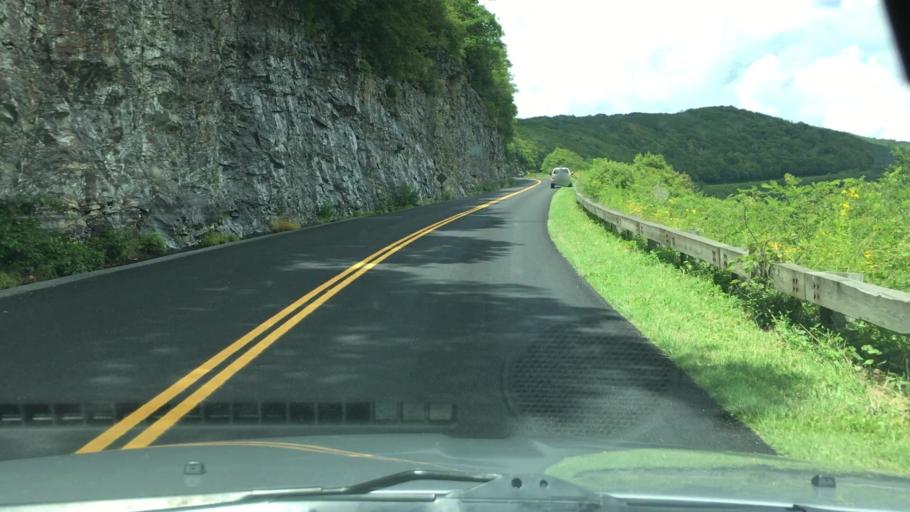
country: US
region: North Carolina
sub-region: Buncombe County
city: Swannanoa
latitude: 35.6889
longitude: -82.3839
